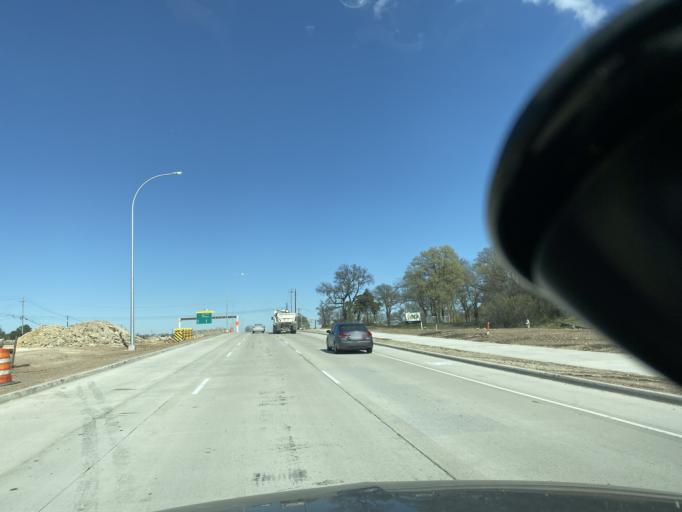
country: US
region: Texas
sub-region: Travis County
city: Austin
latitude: 30.2747
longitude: -97.6676
